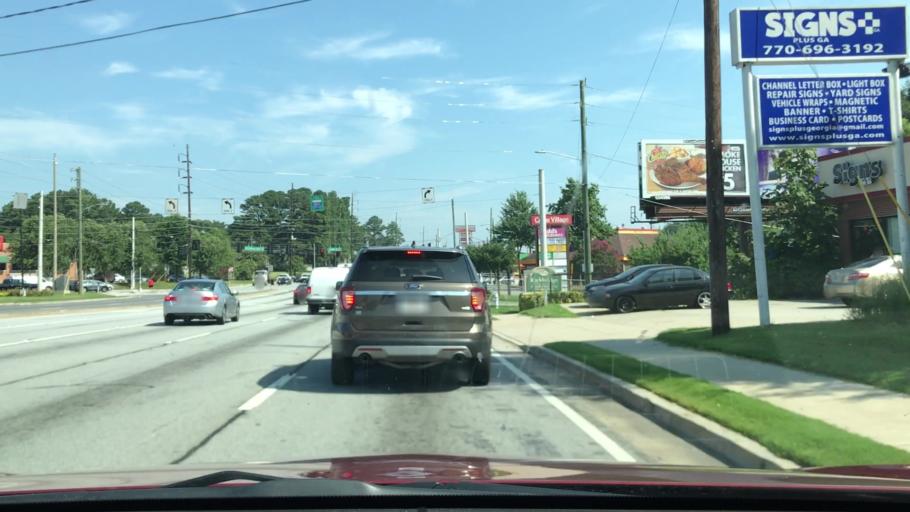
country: US
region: Georgia
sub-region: Gwinnett County
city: Norcross
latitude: 33.9010
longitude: -84.2048
